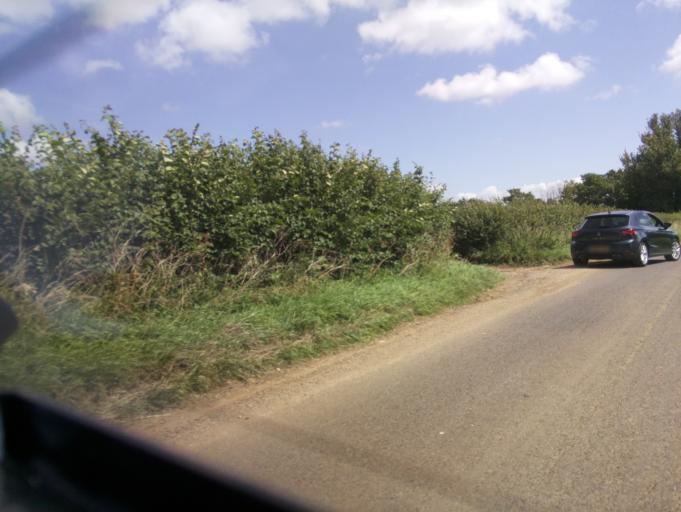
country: GB
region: England
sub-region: Wiltshire
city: Luckington
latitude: 51.5414
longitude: -2.2176
